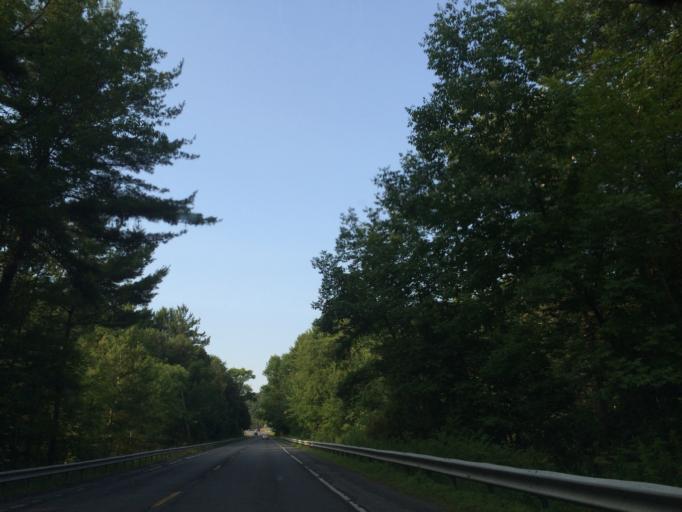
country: US
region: Massachusetts
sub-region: Berkshire County
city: Richmond
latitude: 42.3904
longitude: -73.4155
